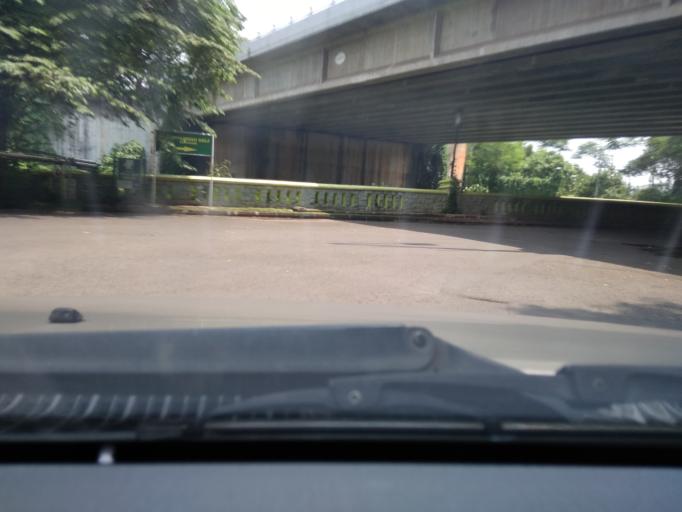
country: ID
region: West Java
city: Serpong
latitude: -6.2822
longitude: 106.6574
